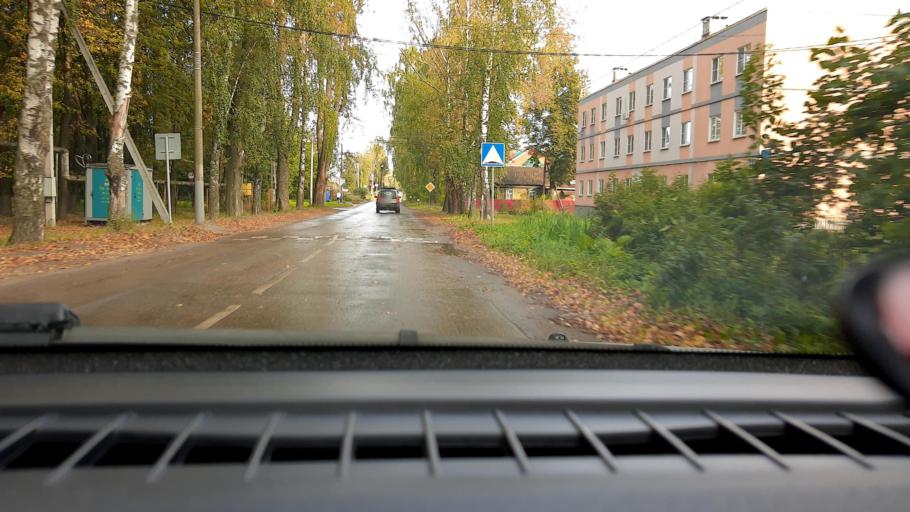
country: RU
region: Nizjnij Novgorod
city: Kstovo
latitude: 56.1848
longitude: 44.1647
